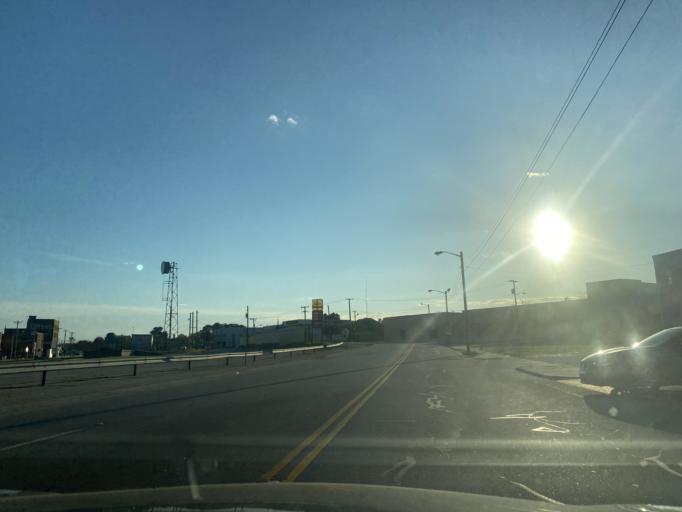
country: US
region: South Carolina
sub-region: Cherokee County
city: Gaffney
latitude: 35.0778
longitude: -81.6457
